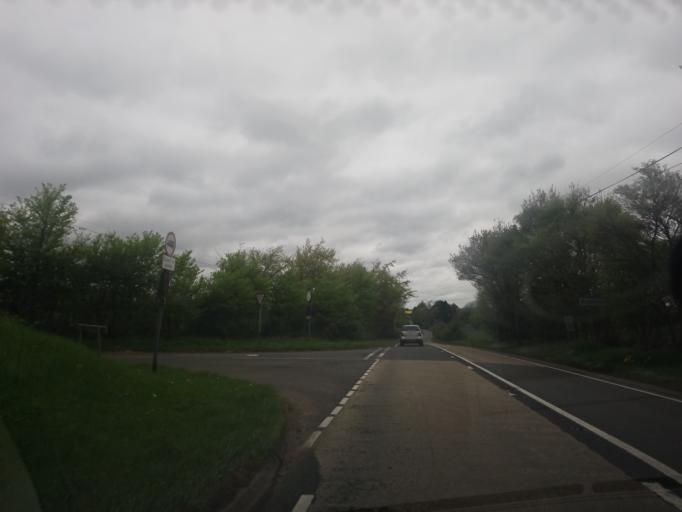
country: GB
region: England
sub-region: Telford and Wrekin
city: Chetwynd
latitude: 52.8075
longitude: -2.4363
